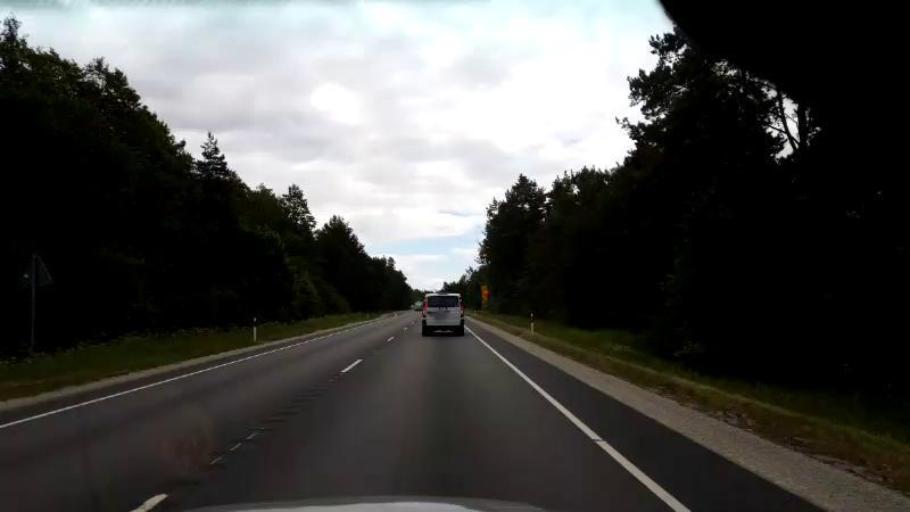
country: EE
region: Paernumaa
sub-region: Paernu linn
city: Parnu
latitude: 58.2094
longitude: 24.4852
